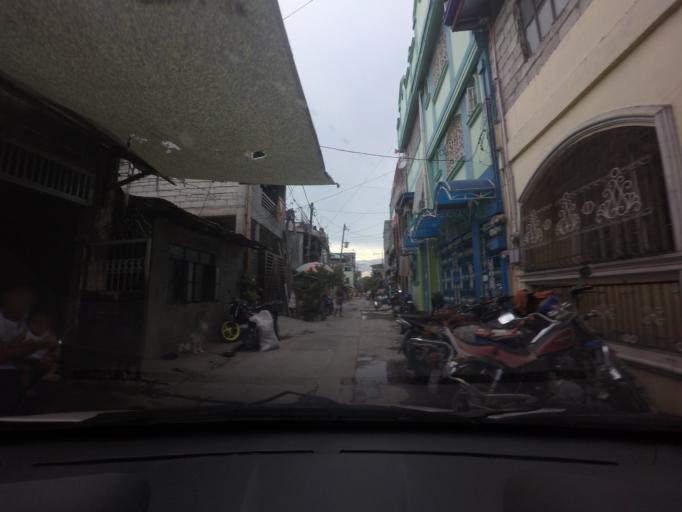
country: PH
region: Calabarzon
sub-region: Province of Rizal
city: Pateros
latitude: 14.5257
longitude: 121.0598
